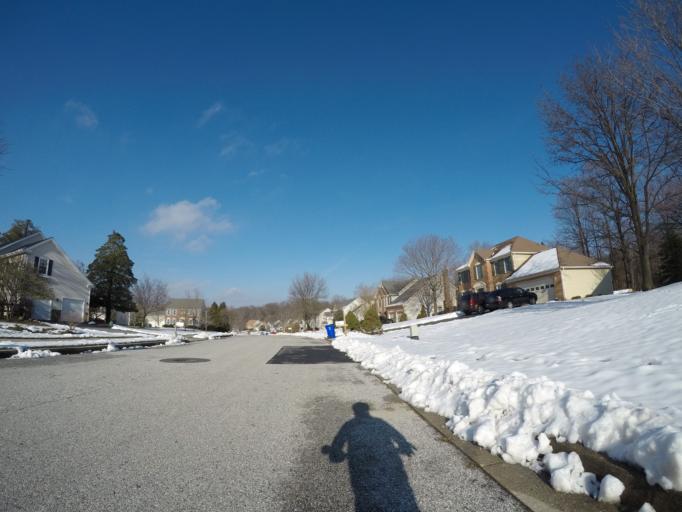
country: US
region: Maryland
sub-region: Howard County
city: Ilchester
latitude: 39.2158
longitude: -76.7760
